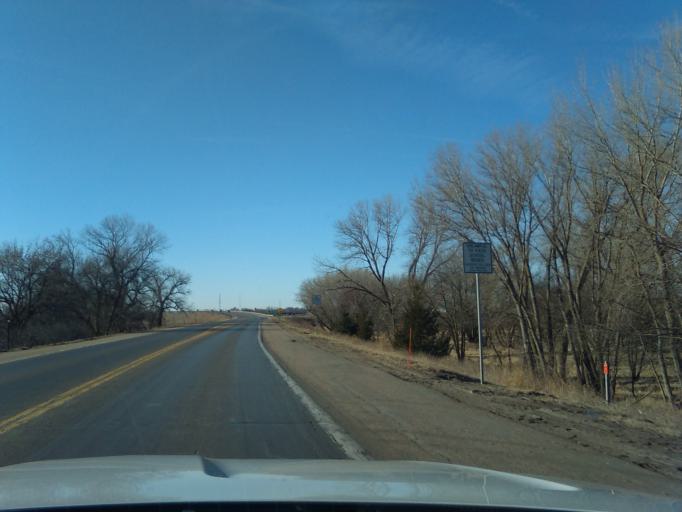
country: US
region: Nebraska
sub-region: Seward County
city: Seward
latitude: 40.9003
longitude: -97.0997
